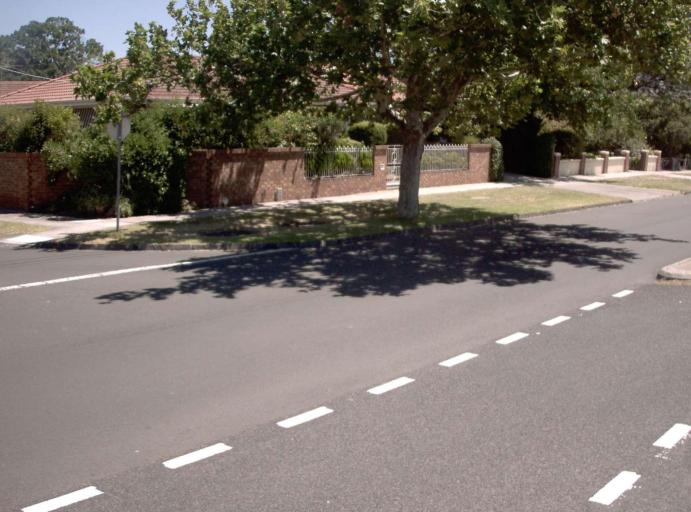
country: AU
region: Victoria
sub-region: Glen Eira
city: Carnegie
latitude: -37.8845
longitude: 145.0610
